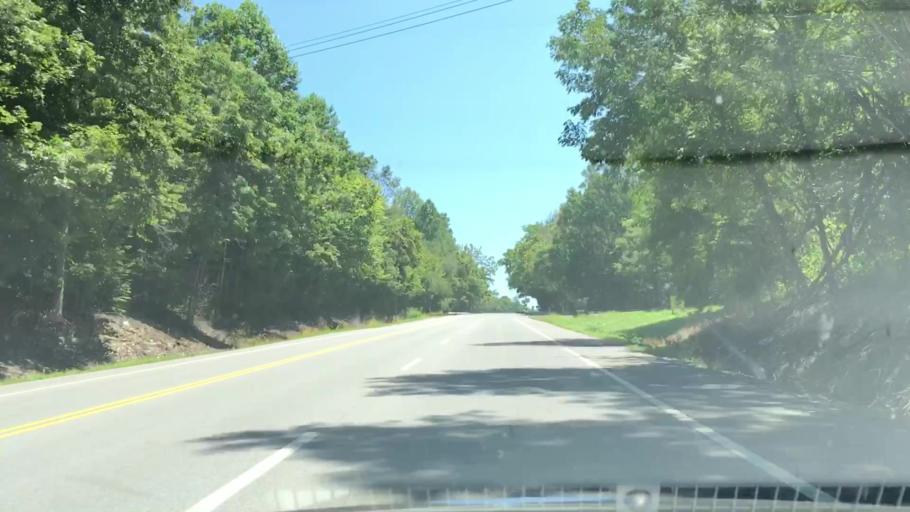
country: US
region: Tennessee
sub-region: Jackson County
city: Gainesboro
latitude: 36.3060
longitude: -85.6430
